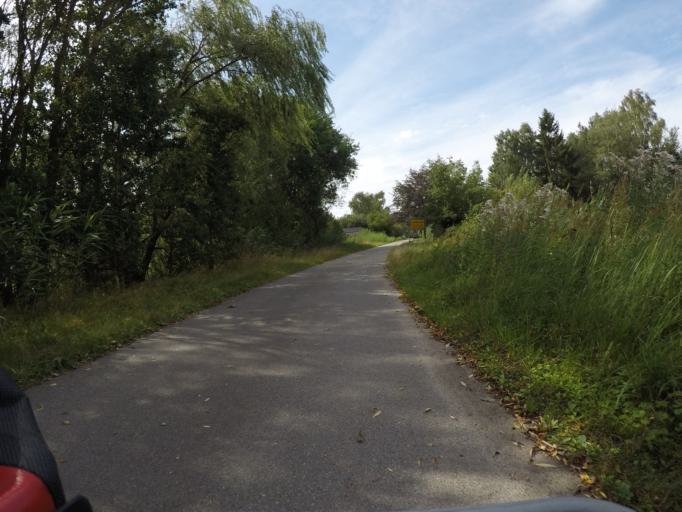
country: DE
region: Lower Saxony
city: Drage
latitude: 53.3697
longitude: 10.2717
